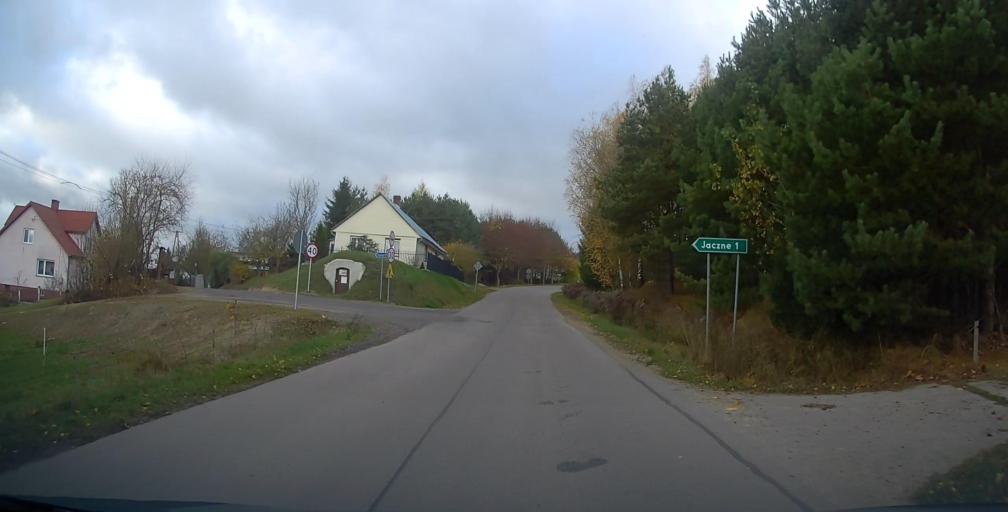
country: PL
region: Podlasie
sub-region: Suwalki
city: Suwalki
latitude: 54.2832
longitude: 22.9024
